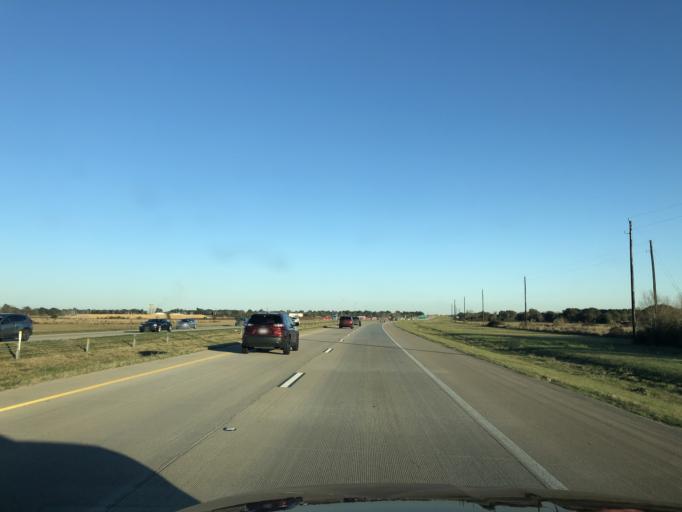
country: US
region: Texas
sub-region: Harris County
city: Cypress
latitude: 30.0545
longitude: -95.7097
